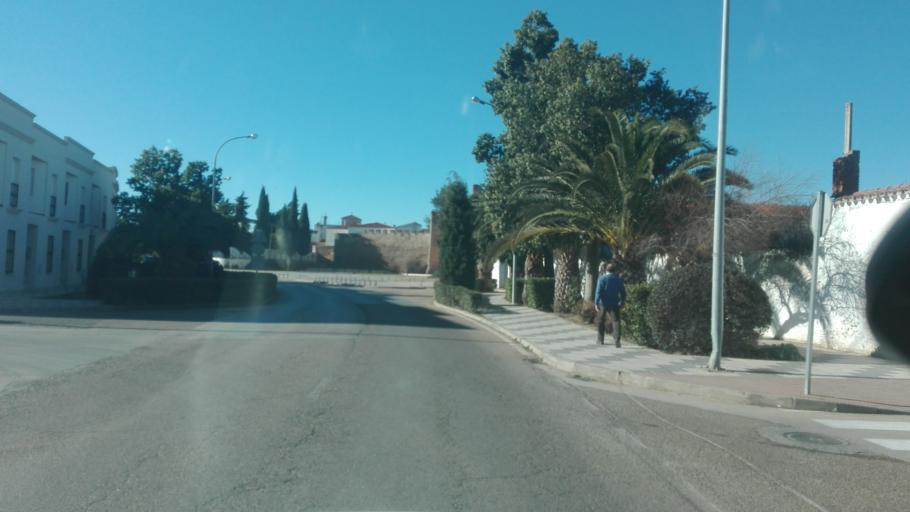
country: ES
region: Extremadura
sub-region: Provincia de Badajoz
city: Llerena
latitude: 38.2370
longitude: -6.0109
